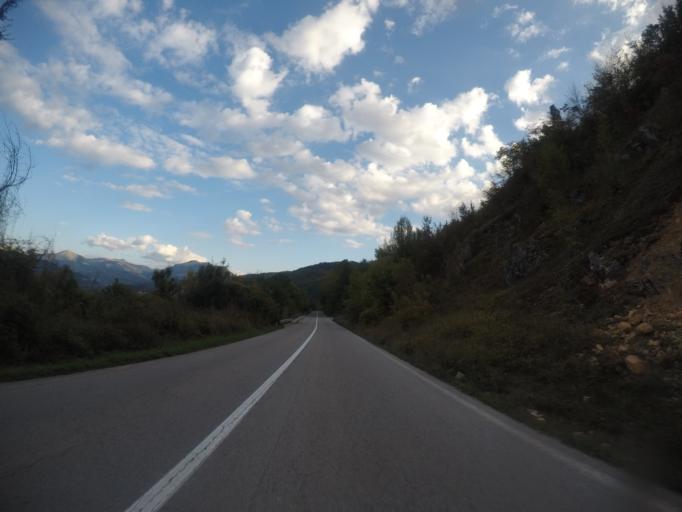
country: ME
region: Mojkovac
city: Mojkovac
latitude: 42.9825
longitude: 19.5172
